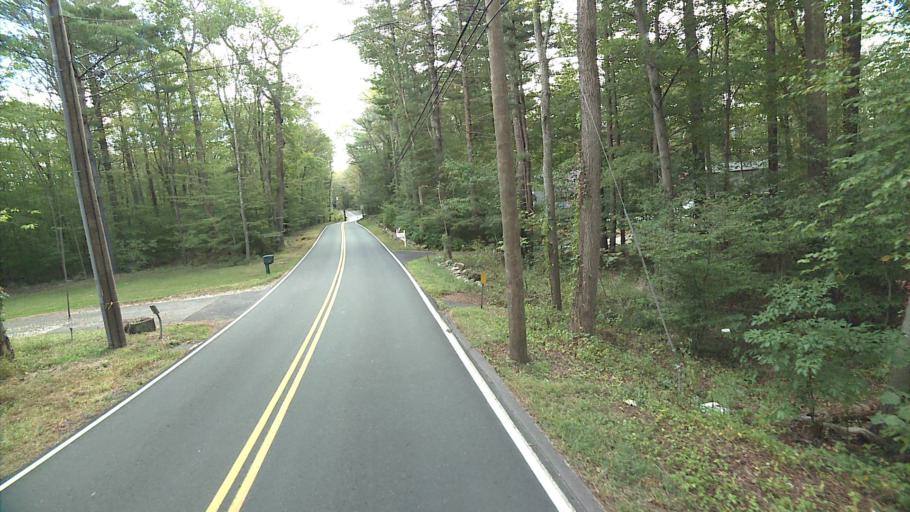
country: US
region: Connecticut
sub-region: New Haven County
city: Madison
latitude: 41.3866
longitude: -72.5952
